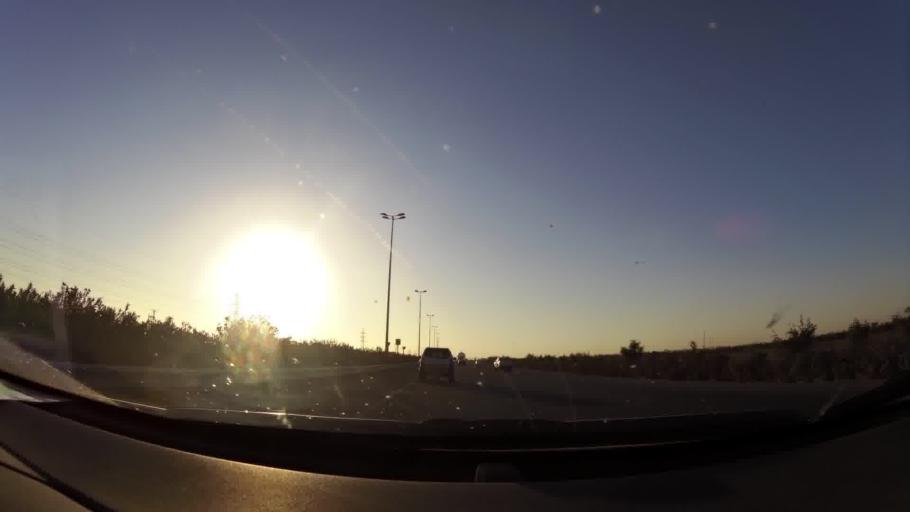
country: KW
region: Al Ahmadi
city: Al Fahahil
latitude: 28.9809
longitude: 48.1548
